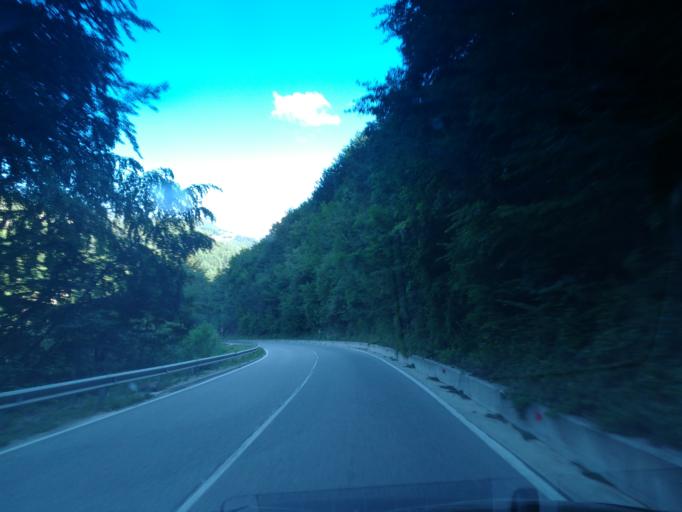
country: BG
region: Smolyan
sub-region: Obshtina Chepelare
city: Chepelare
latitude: 41.8086
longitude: 24.7074
